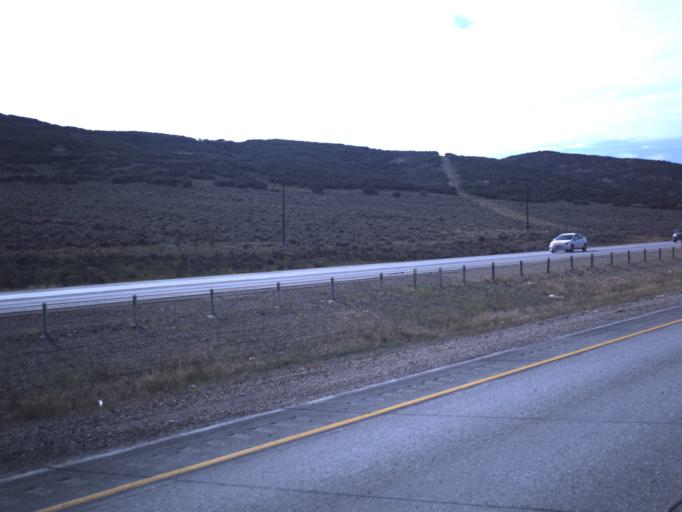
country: US
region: Utah
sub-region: Summit County
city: Park City
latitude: 40.6902
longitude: -111.4667
